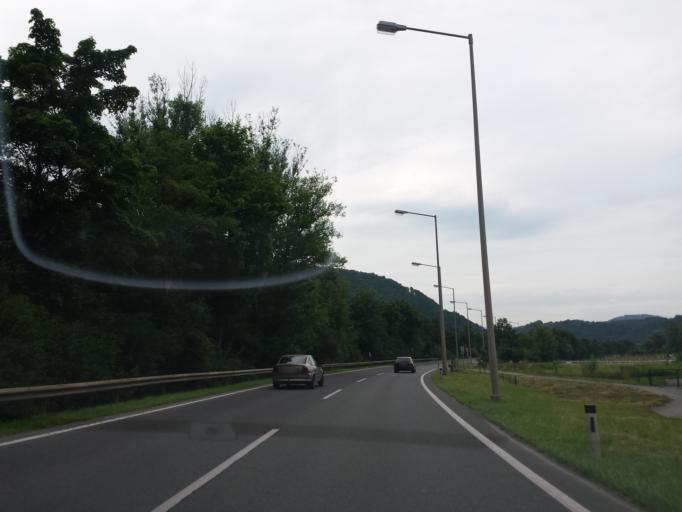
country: AT
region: Styria
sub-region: Graz Stadt
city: Goesting
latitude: 47.1075
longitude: 15.3807
